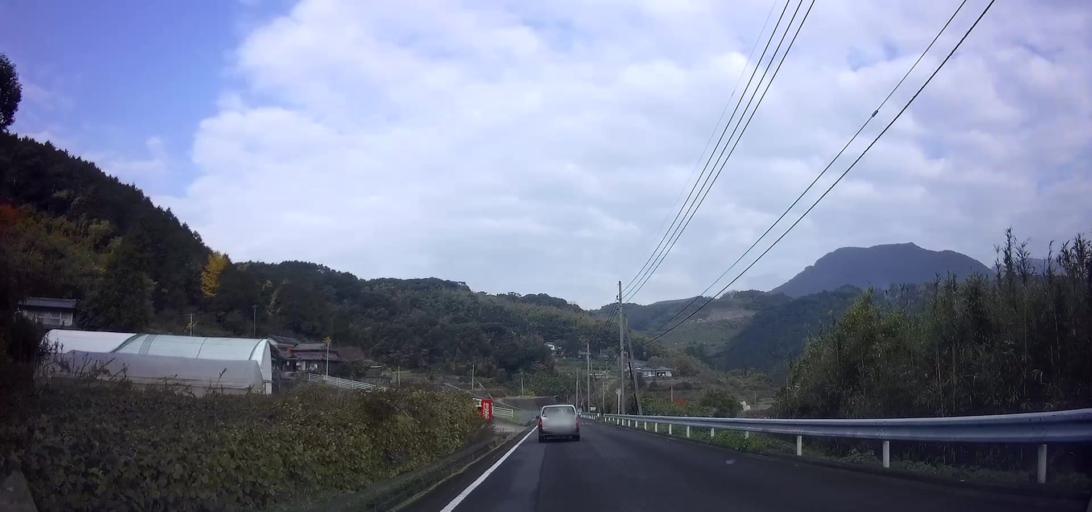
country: JP
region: Nagasaki
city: Shimabara
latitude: 32.6852
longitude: 130.2747
